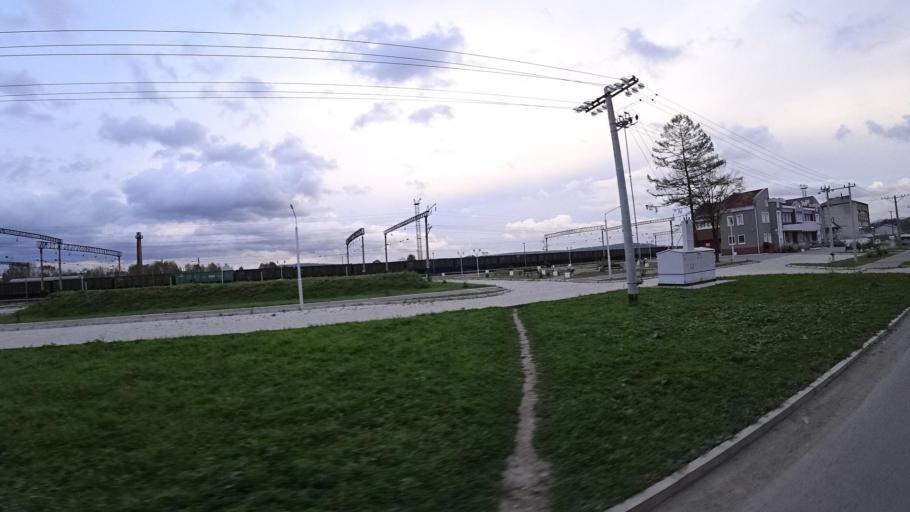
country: RU
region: Jewish Autonomous Oblast
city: Izvestkovyy
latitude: 48.9834
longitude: 131.5552
